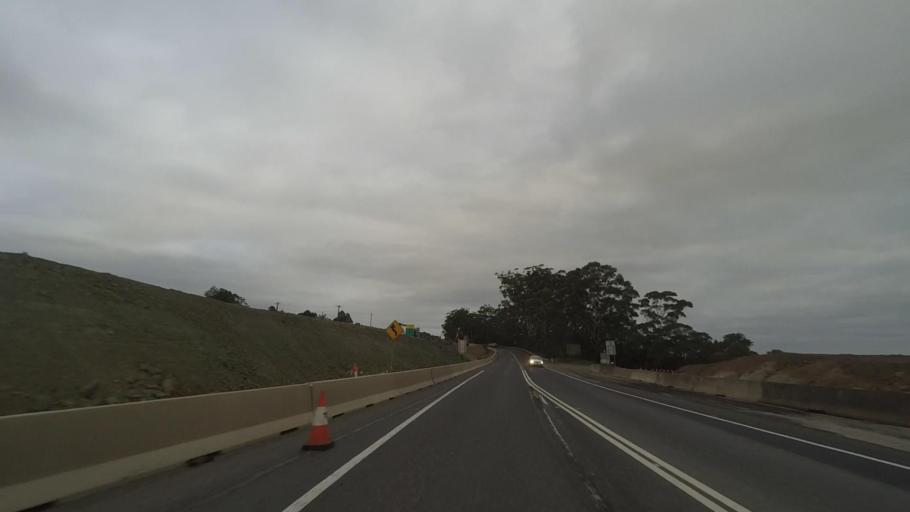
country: AU
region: New South Wales
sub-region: Shoalhaven Shire
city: Berry
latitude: -34.7689
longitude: 150.7127
